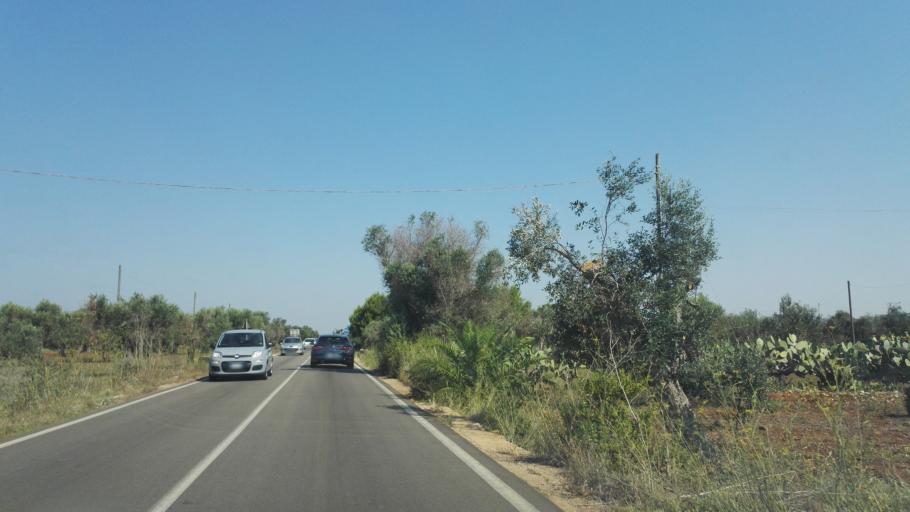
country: IT
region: Apulia
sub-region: Provincia di Lecce
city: Nardo
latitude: 40.1763
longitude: 17.9786
